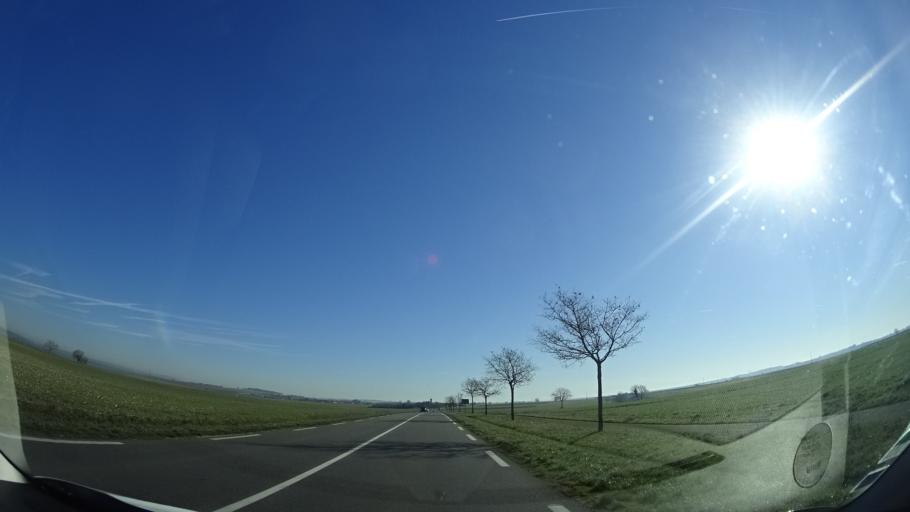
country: FR
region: Poitou-Charentes
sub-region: Departement de la Vienne
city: Avanton
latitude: 46.6866
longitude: 0.2923
